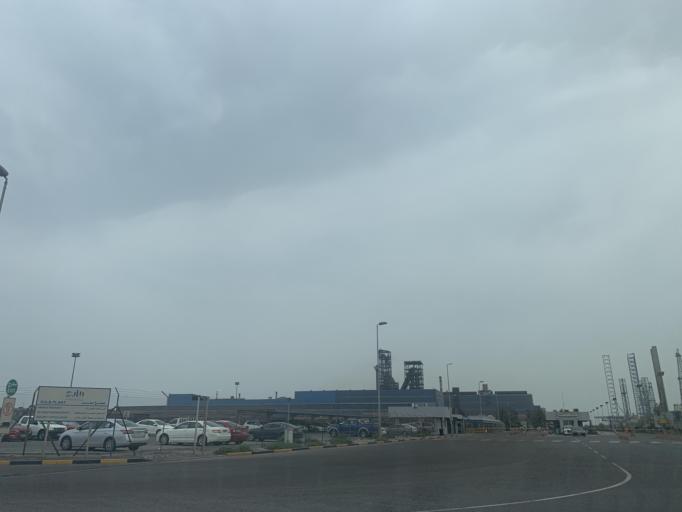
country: BH
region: Muharraq
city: Al Hadd
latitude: 26.2028
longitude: 50.6732
